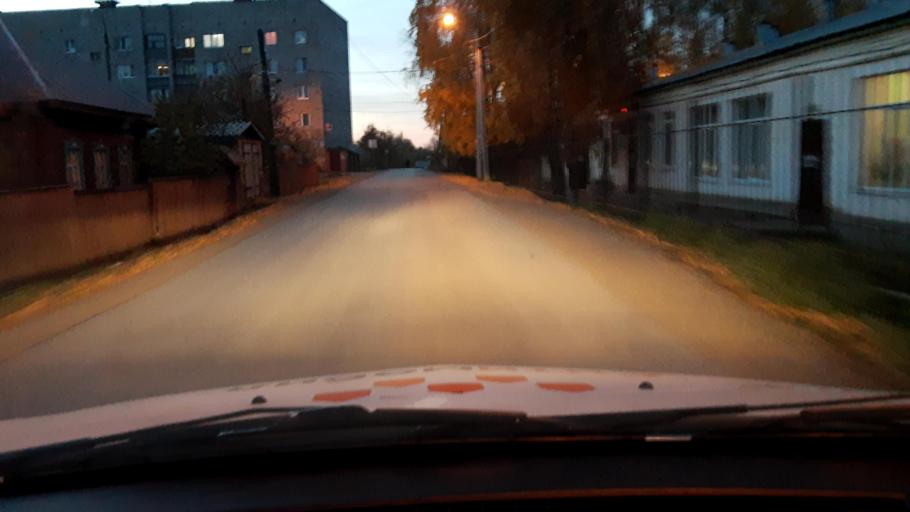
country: RU
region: Bashkortostan
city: Iglino
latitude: 54.7641
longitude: 56.2283
